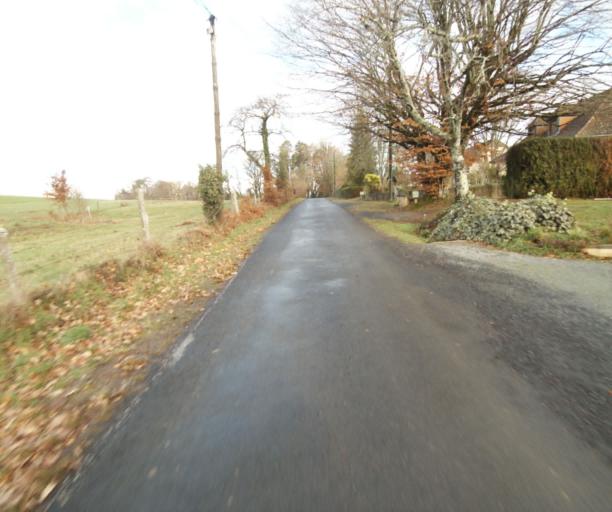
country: FR
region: Limousin
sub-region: Departement de la Correze
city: Saint-Mexant
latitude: 45.2512
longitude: 1.6328
